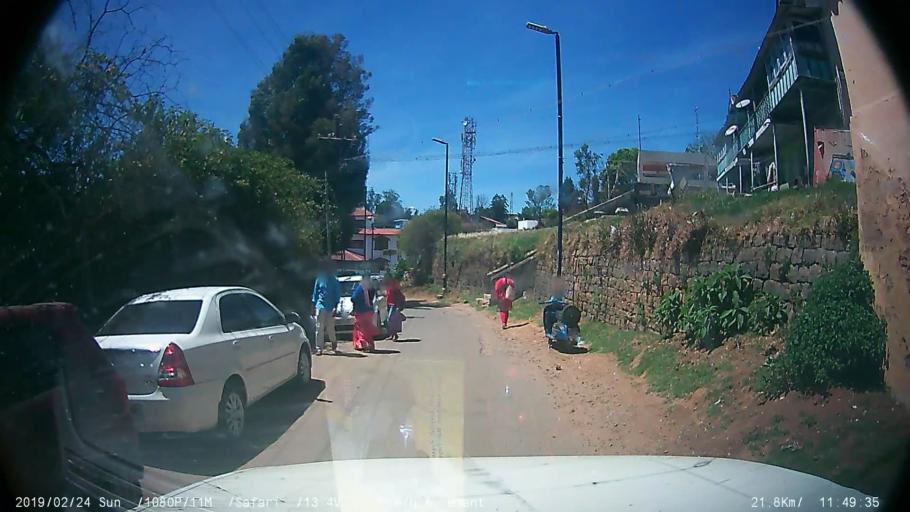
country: IN
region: Tamil Nadu
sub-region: Nilgiri
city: Ooty
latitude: 11.4169
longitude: 76.7092
